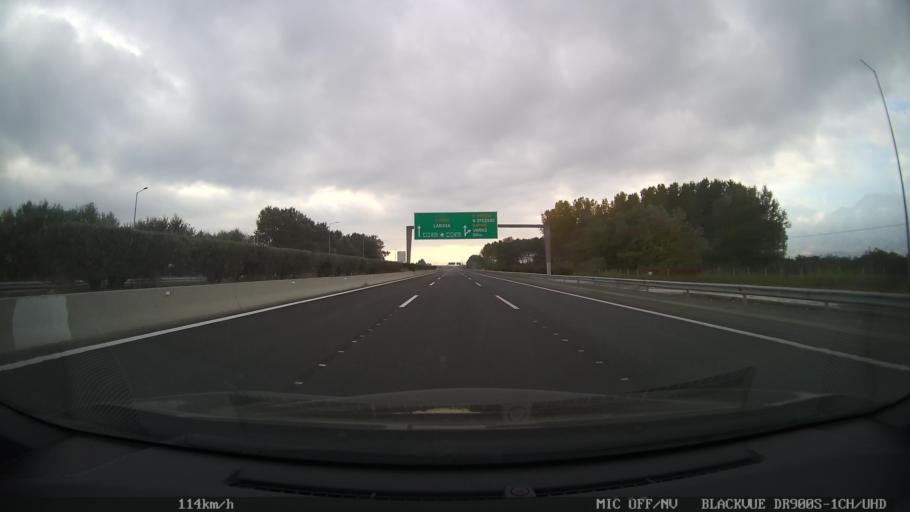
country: GR
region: Central Macedonia
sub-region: Nomos Pierias
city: Nea Efesos
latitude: 40.2030
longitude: 22.5464
